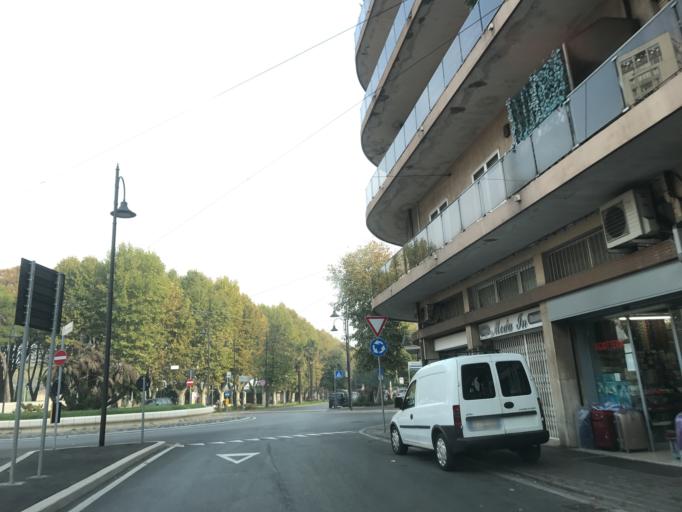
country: IT
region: Emilia-Romagna
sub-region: Provincia di Rimini
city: Rimini
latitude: 44.0653
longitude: 12.5698
